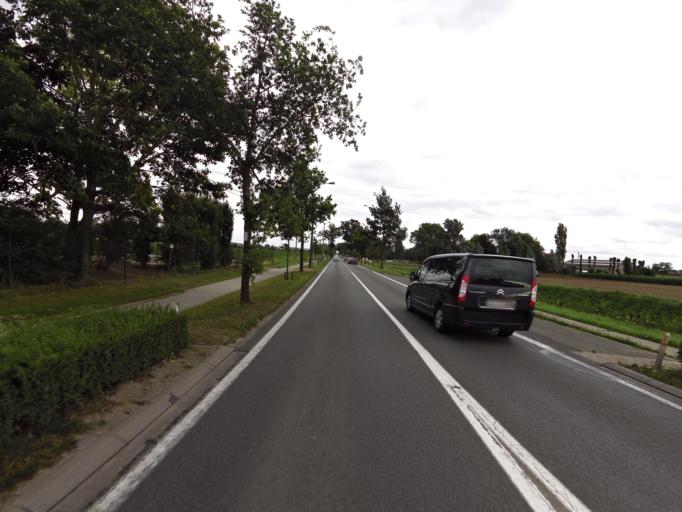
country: BE
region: Flanders
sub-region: Provincie West-Vlaanderen
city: Hooglede
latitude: 50.9555
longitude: 3.0875
